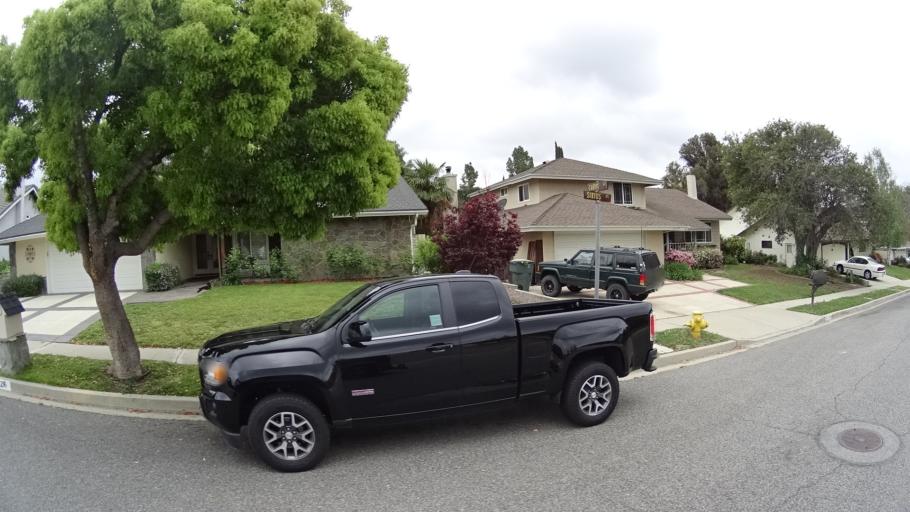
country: US
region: California
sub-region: Ventura County
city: Thousand Oaks
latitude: 34.2152
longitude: -118.8845
